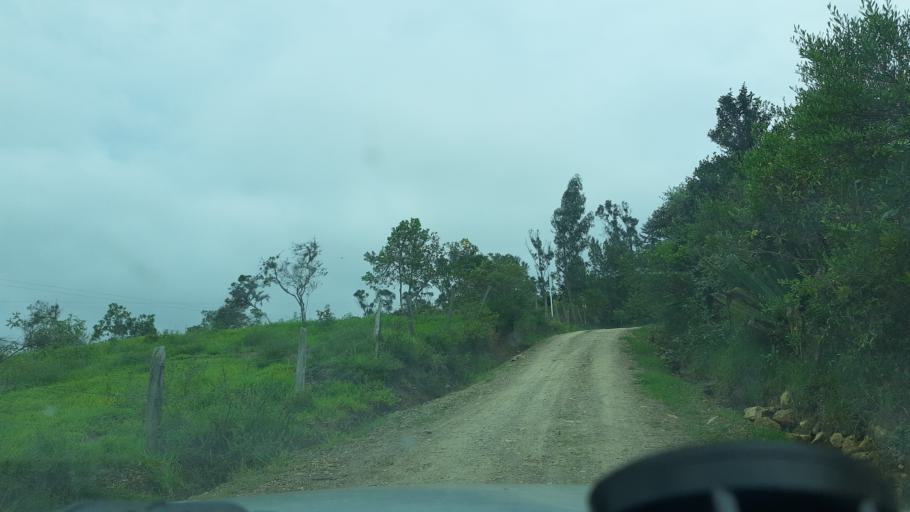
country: CO
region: Boyaca
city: Santa Sofia
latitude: 5.7110
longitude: -73.5881
